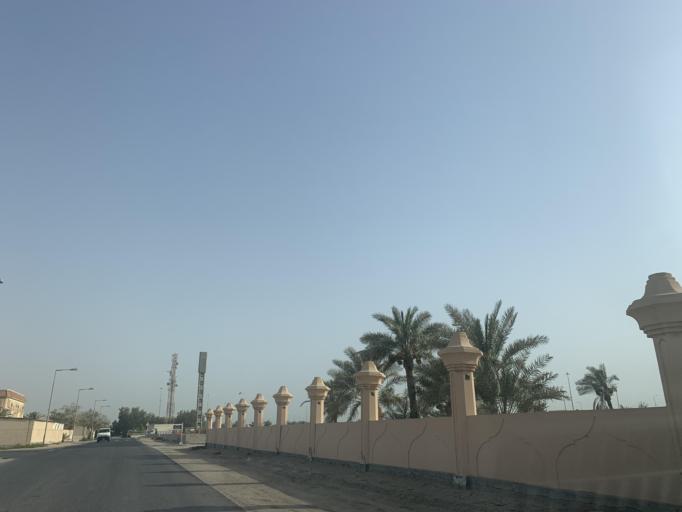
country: BH
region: Central Governorate
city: Madinat Hamad
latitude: 26.1769
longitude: 50.4677
